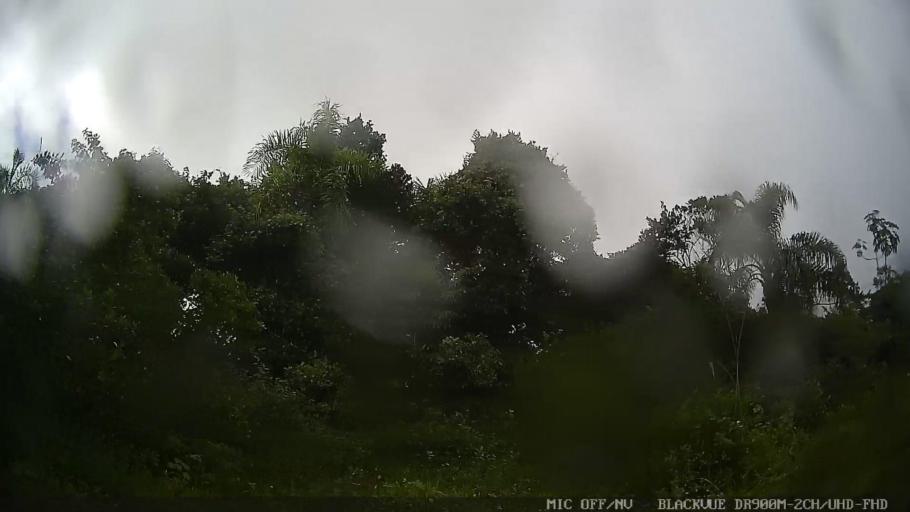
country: BR
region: Sao Paulo
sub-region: Peruibe
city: Peruibe
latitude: -24.2503
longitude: -46.9004
